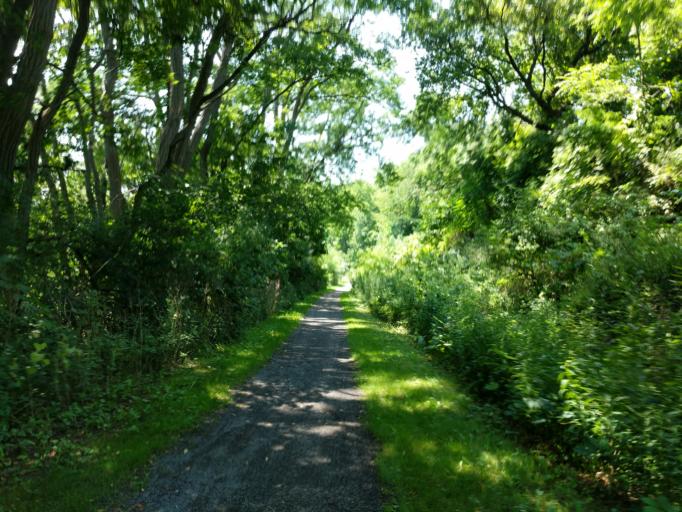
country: US
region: New York
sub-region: Yates County
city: Penn Yan
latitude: 42.6809
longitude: -76.9600
